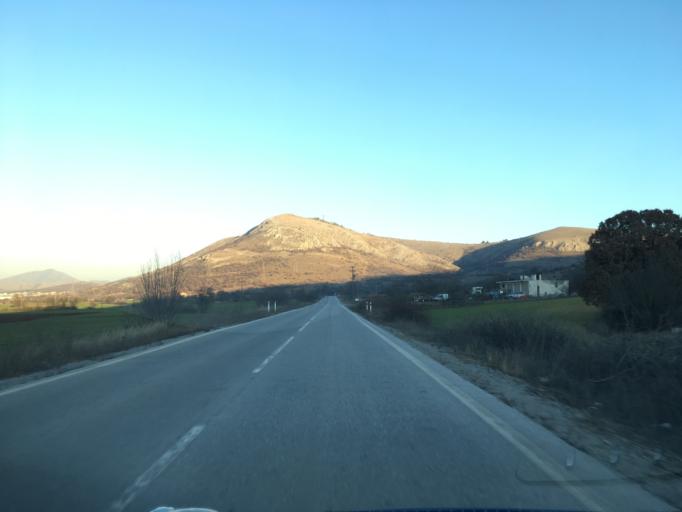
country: GR
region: West Macedonia
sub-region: Nomos Kozanis
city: Kozani
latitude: 40.3170
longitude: 21.7504
